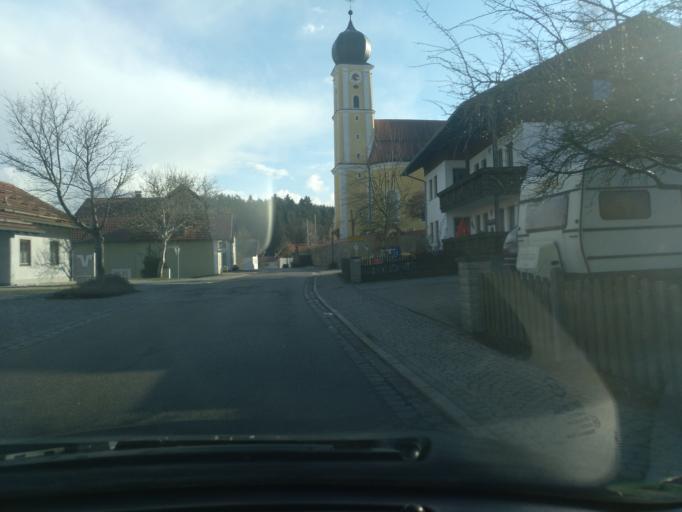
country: DE
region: Bavaria
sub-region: Upper Palatinate
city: Zandt
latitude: 49.1352
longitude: 12.7154
